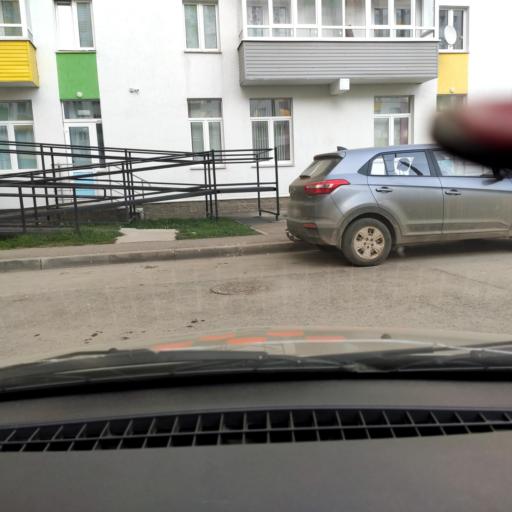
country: RU
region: Bashkortostan
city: Ufa
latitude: 54.6865
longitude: 55.9821
